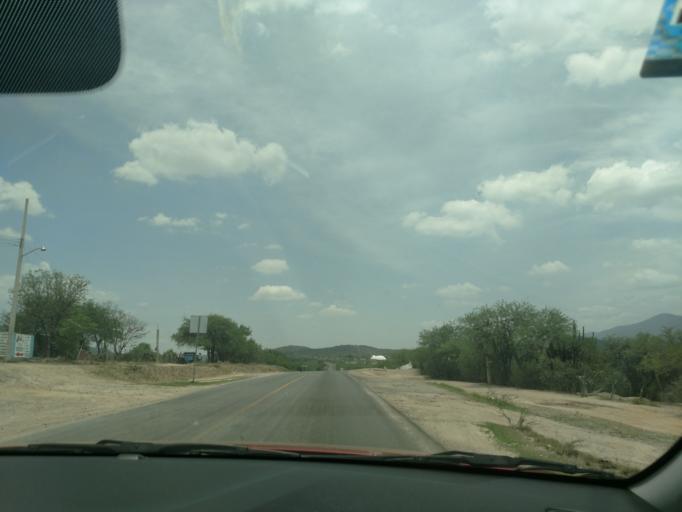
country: MX
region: San Luis Potosi
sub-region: Rioverde
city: Progreso
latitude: 22.0183
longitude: -100.3713
